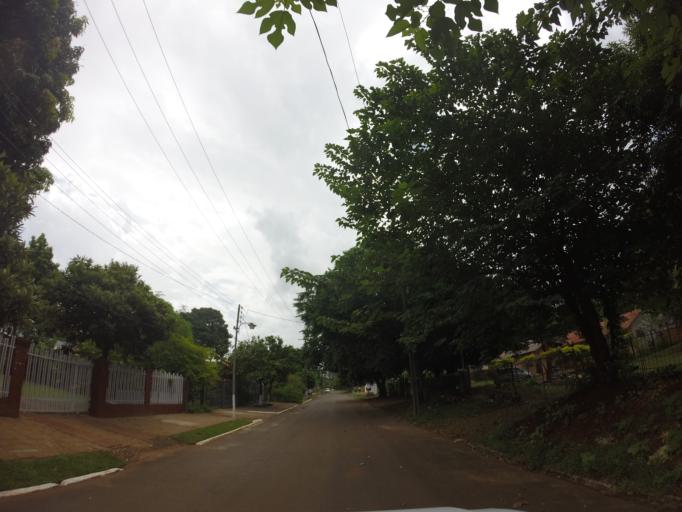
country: PY
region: Alto Parana
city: Ciudad del Este
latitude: -25.4138
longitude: -54.6257
